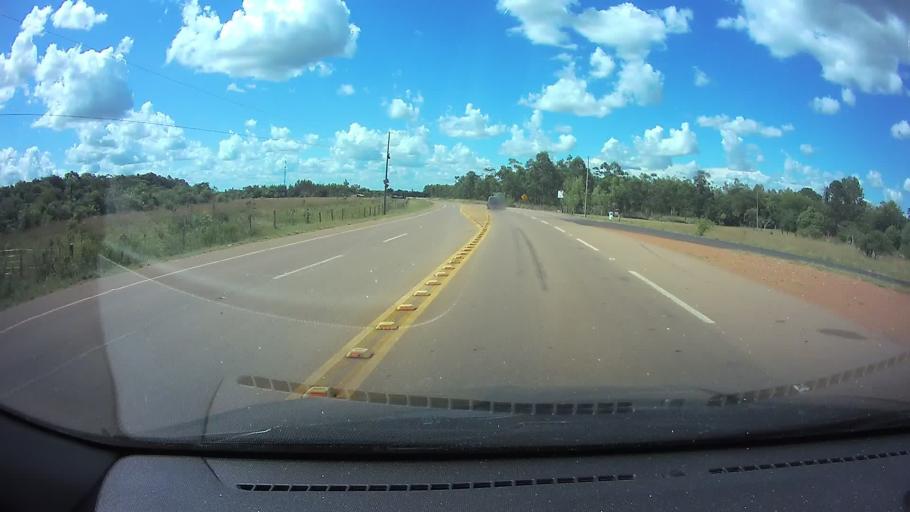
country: PY
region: Guaira
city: Itape
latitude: -25.9092
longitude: -56.6752
